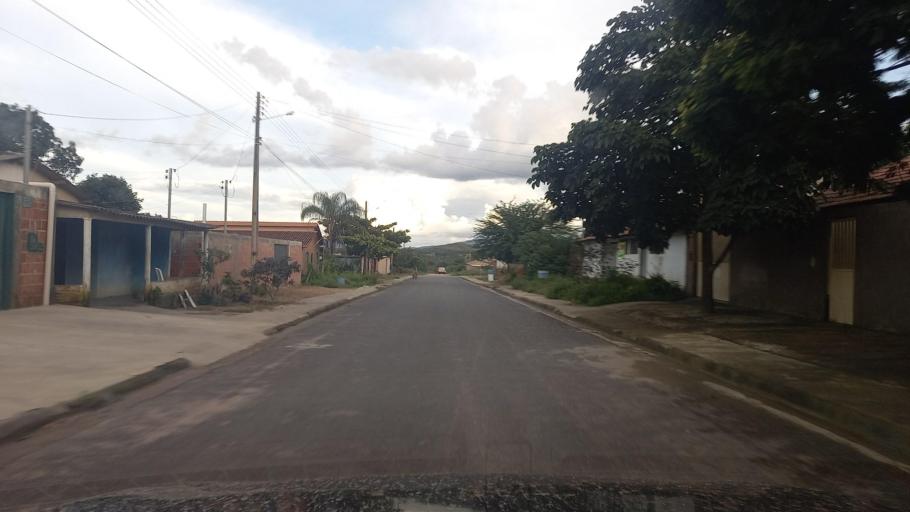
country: BR
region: Goias
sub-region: Cavalcante
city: Cavalcante
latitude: -13.7907
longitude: -47.4559
